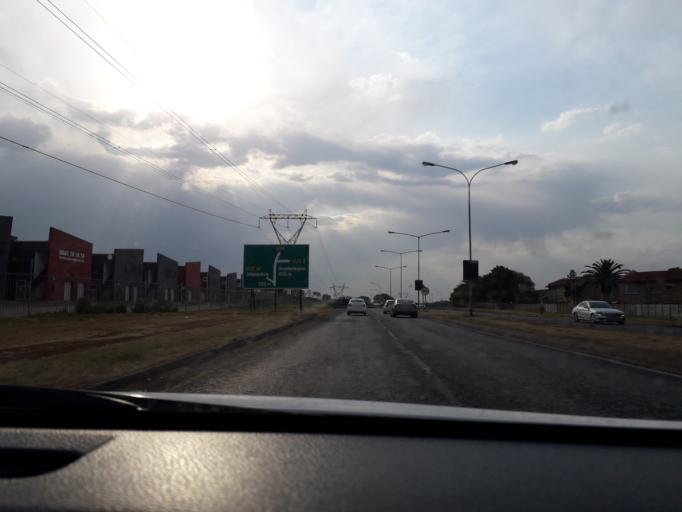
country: ZA
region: Gauteng
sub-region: City of Johannesburg Metropolitan Municipality
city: Modderfontein
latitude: -26.0944
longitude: 28.1965
